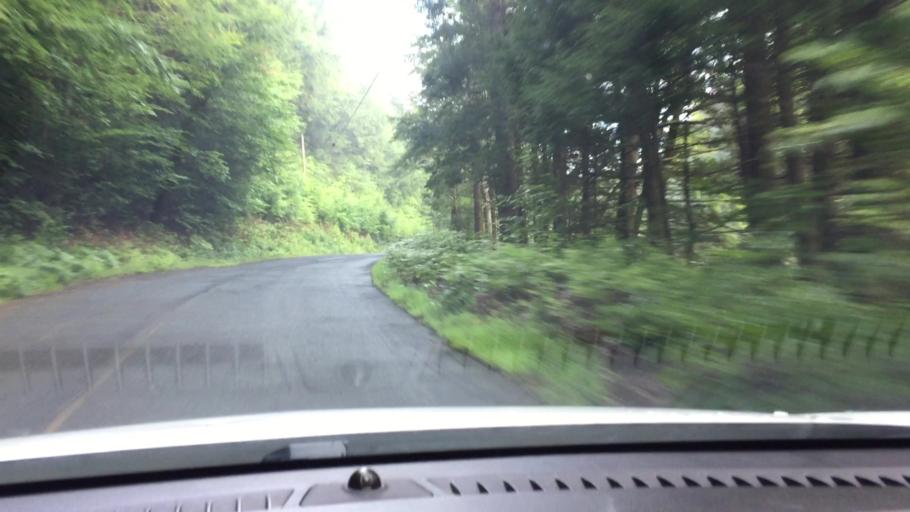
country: US
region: Massachusetts
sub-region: Hampshire County
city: Chesterfield
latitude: 42.3073
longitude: -72.9103
